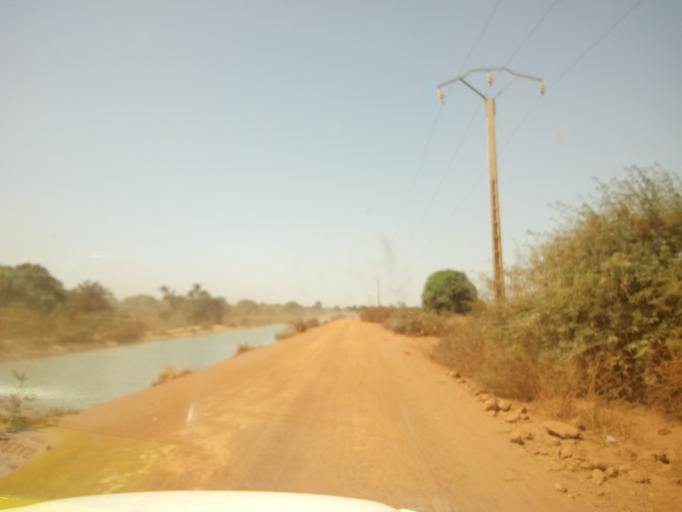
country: ML
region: Bamako
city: Bamako
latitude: 12.6242
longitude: -7.7557
